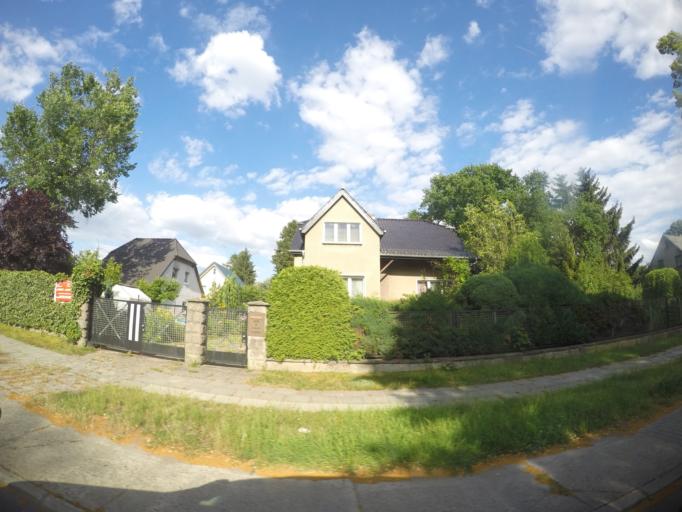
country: DE
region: Berlin
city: Biesdorf
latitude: 52.4854
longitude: 13.5603
